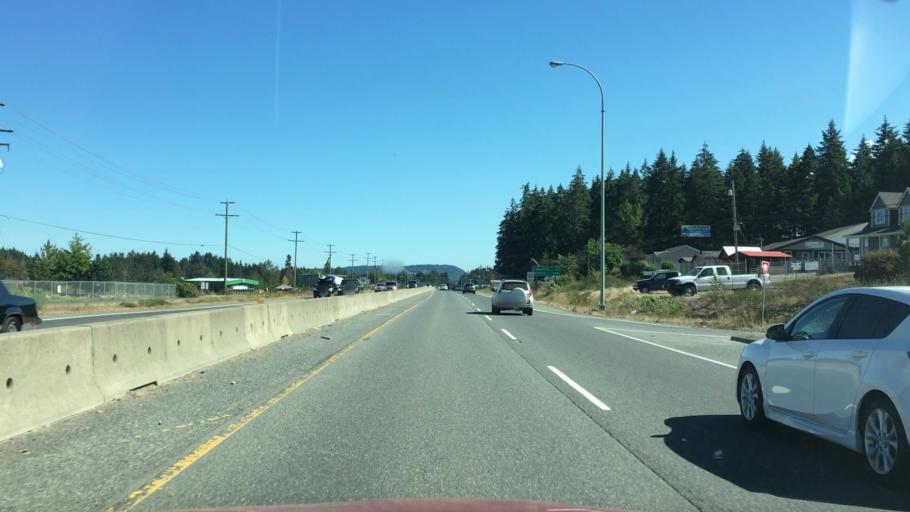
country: CA
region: British Columbia
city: Nanaimo
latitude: 49.1029
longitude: -123.8929
